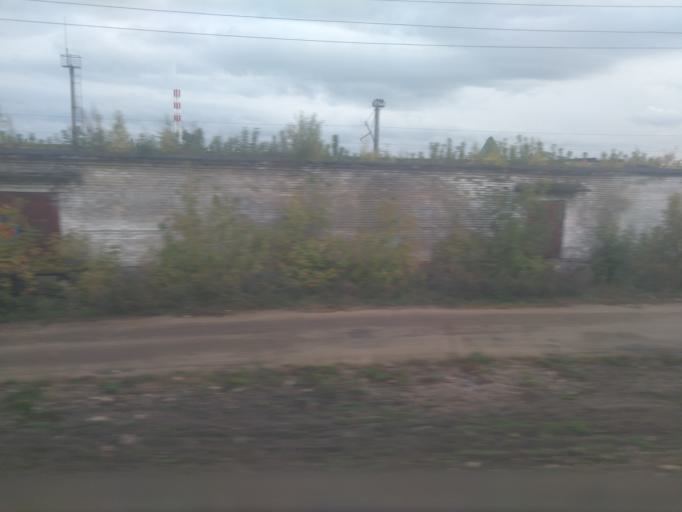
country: RU
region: Tatarstan
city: Staroye Arakchino
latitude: 55.8165
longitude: 48.9041
